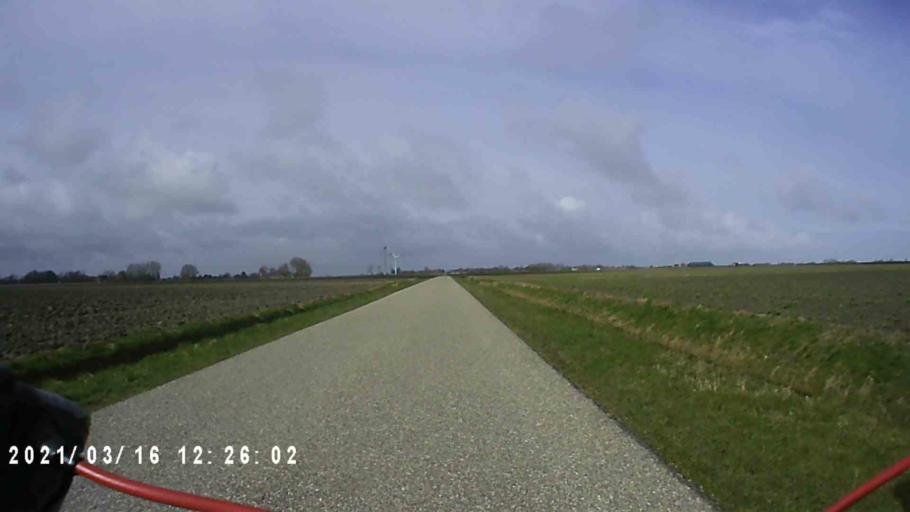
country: NL
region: Friesland
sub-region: Gemeente Leeuwarderadeel
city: Stiens
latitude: 53.2966
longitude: 5.7462
